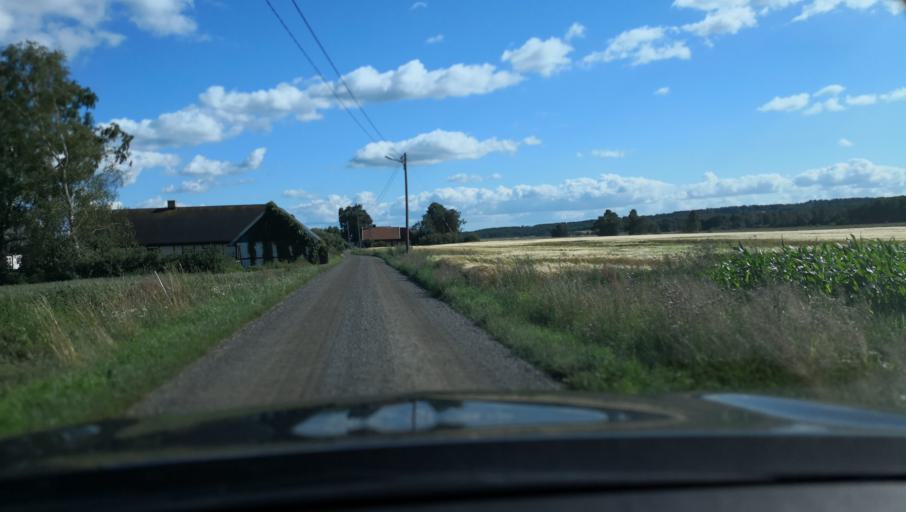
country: SE
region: Skane
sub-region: Kristianstads Kommun
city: Degeberga
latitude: 55.8101
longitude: 14.1891
